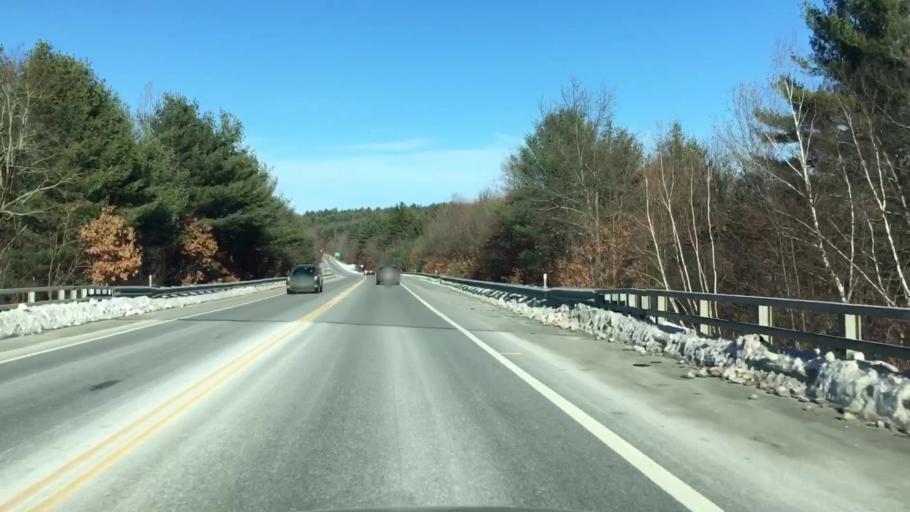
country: US
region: New Hampshire
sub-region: Hillsborough County
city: Milford
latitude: 42.8454
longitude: -71.6154
